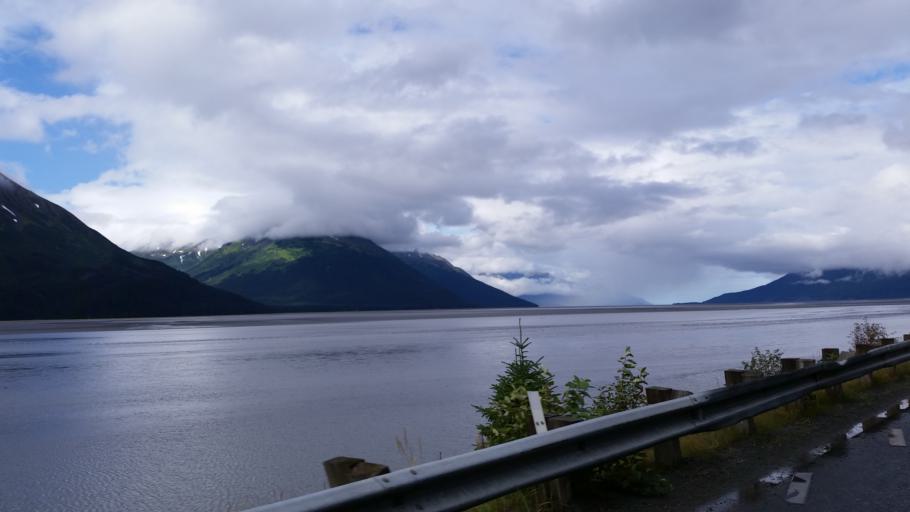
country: US
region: Alaska
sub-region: Anchorage Municipality
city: Girdwood
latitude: 60.8899
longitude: -149.0573
